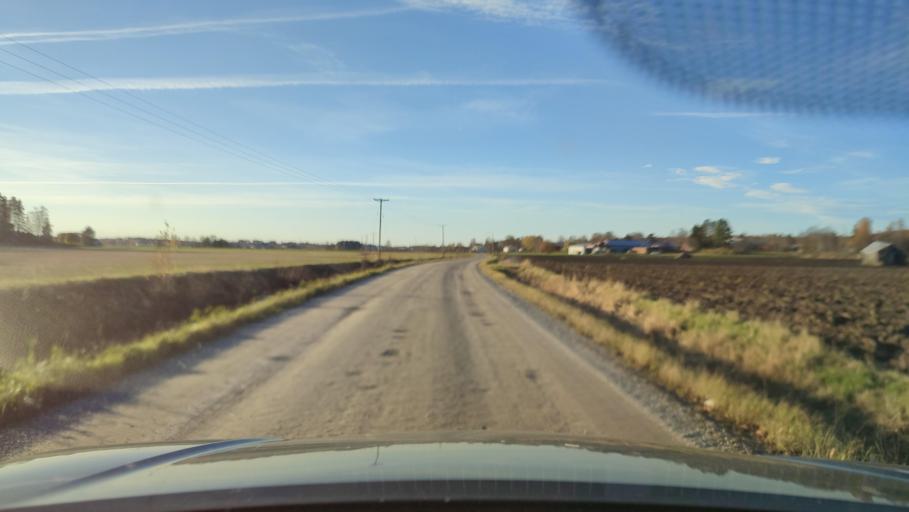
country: FI
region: Ostrobothnia
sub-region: Vaasa
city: Ristinummi
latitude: 63.0103
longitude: 21.7064
